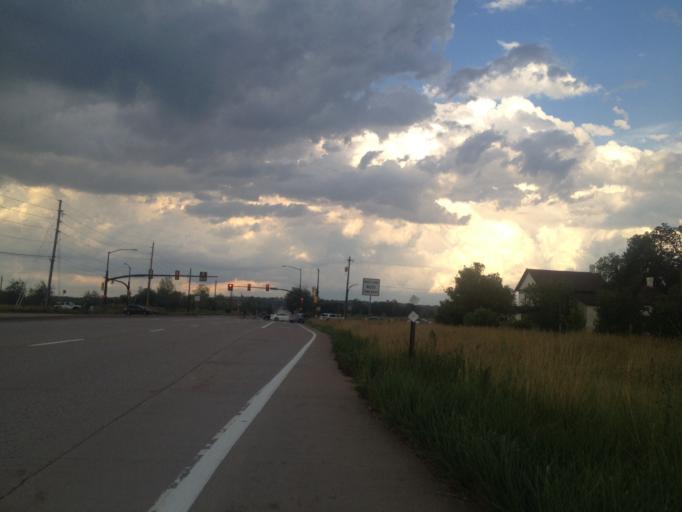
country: US
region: Colorado
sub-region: Boulder County
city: Superior
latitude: 39.9860
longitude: -105.2142
